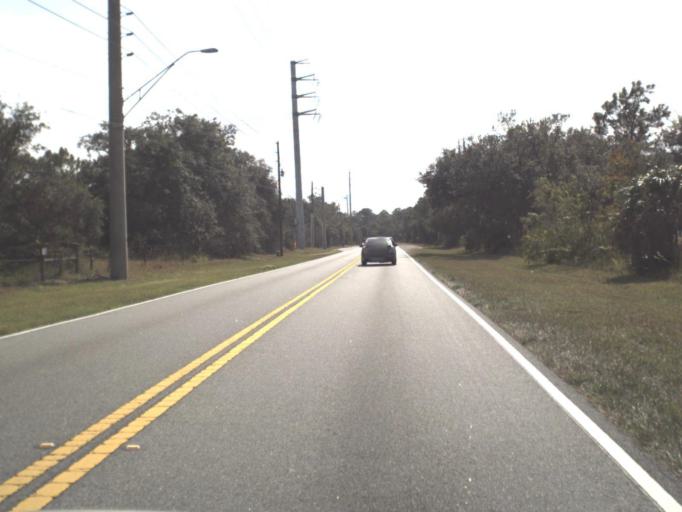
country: US
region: Florida
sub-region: Osceola County
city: Poinciana
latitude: 28.1948
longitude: -81.4689
